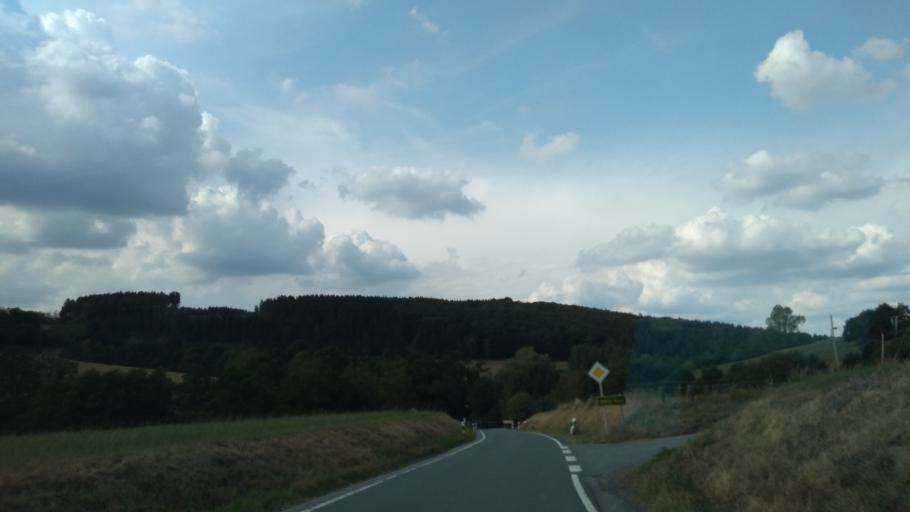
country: DE
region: North Rhine-Westphalia
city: Balve
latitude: 51.2774
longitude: 7.8775
